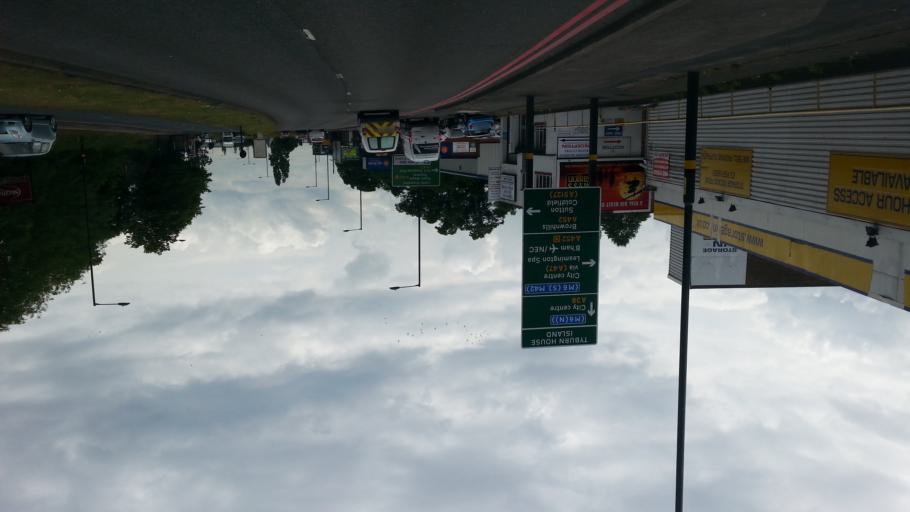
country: GB
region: England
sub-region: City and Borough of Birmingham
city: Sutton Coldfield
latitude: 52.5204
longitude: -1.7978
